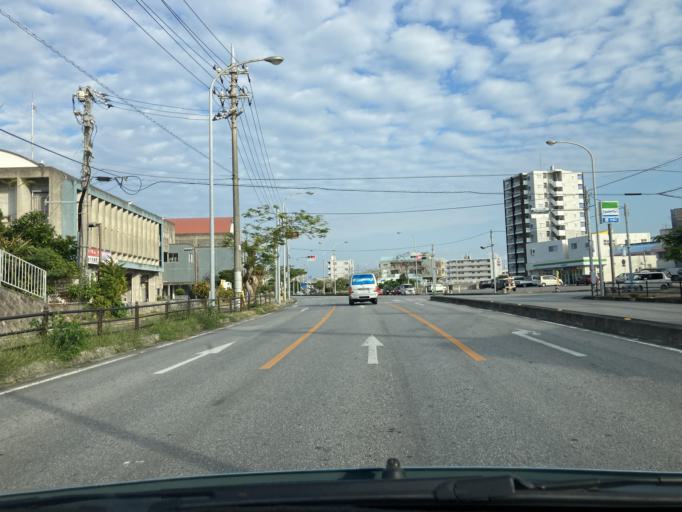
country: JP
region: Okinawa
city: Okinawa
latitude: 26.3535
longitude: 127.8085
